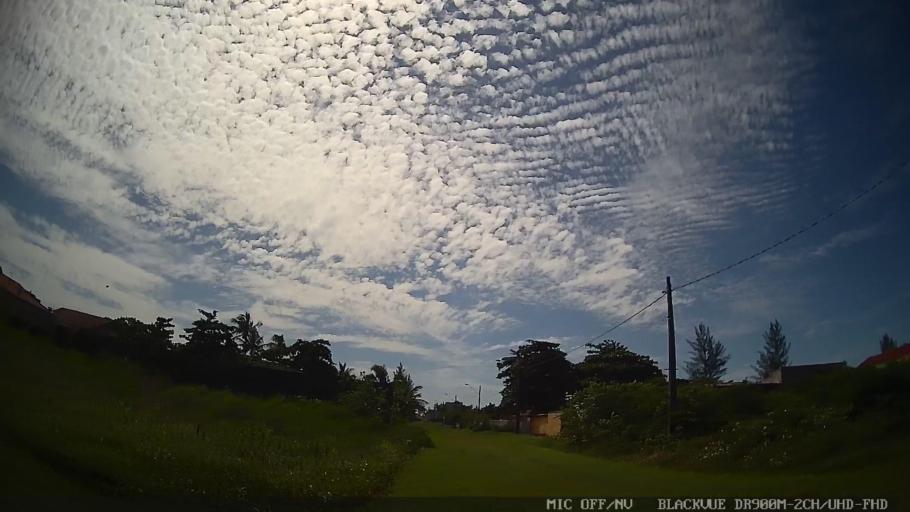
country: BR
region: Sao Paulo
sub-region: Iguape
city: Iguape
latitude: -24.7948
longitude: -47.6232
